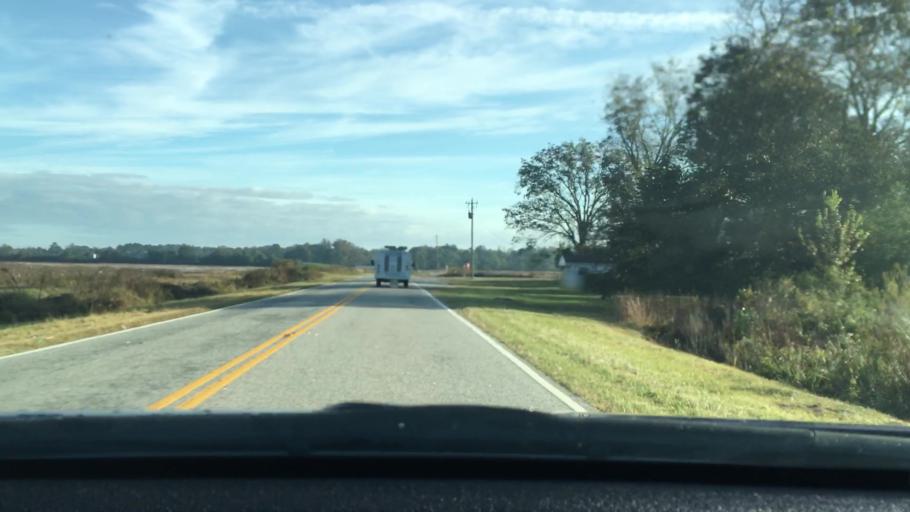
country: US
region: South Carolina
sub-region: Lee County
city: Bishopville
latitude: 34.0704
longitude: -80.2117
